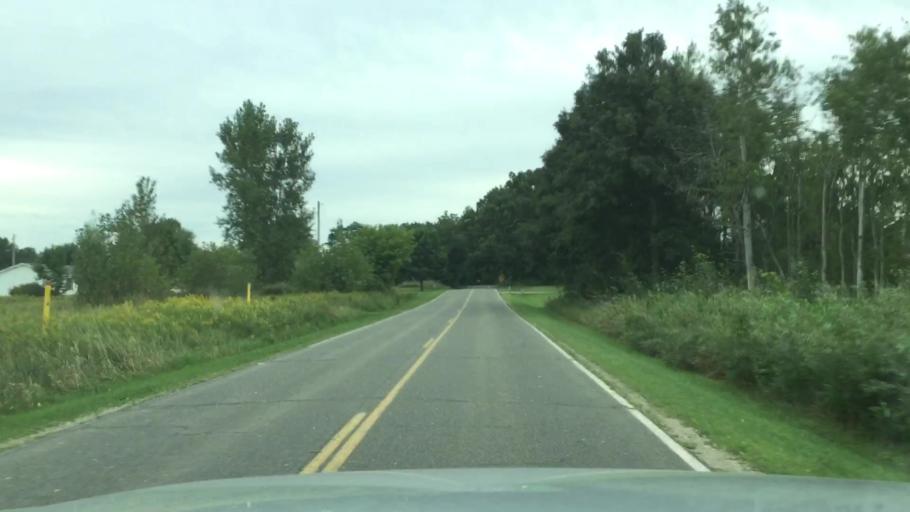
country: US
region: Michigan
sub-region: Shiawassee County
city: Durand
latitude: 42.8398
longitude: -84.0337
